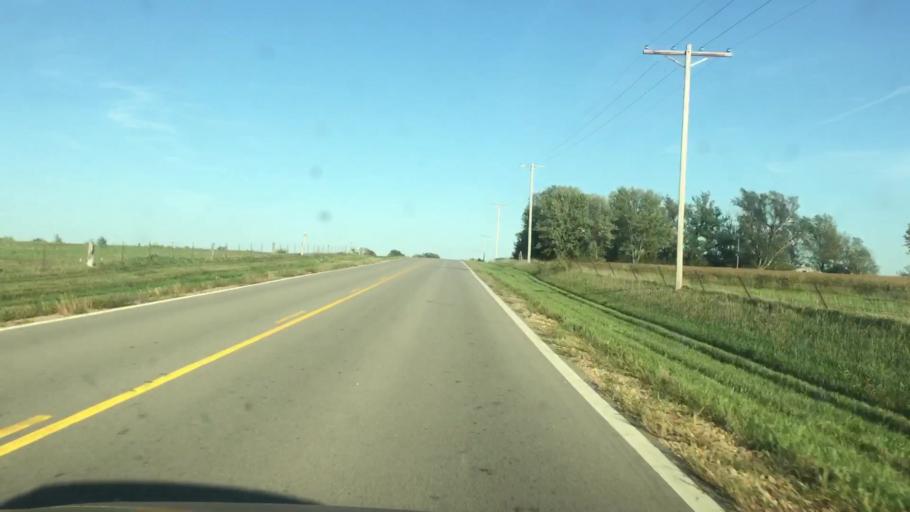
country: US
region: Kansas
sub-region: Brown County
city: Horton
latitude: 39.5876
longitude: -95.5947
